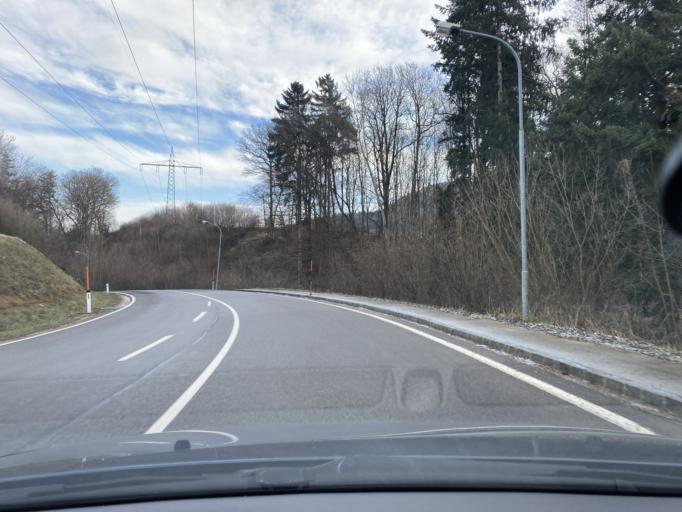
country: AT
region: Lower Austria
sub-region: Politischer Bezirk Melk
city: Loosdorf
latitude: 48.1697
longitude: 15.3688
